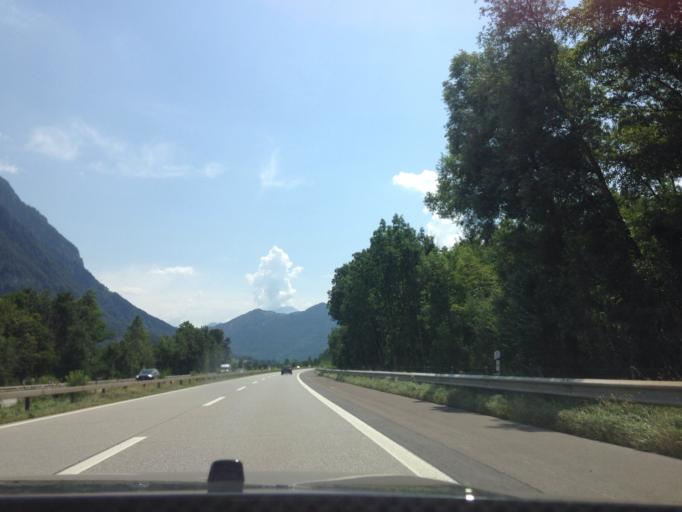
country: LI
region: Triesen
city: Triesen
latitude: 47.0966
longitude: 9.5176
